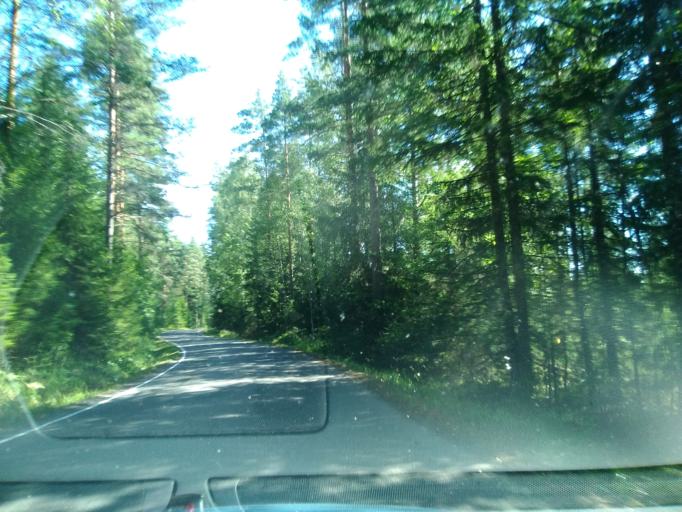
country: FI
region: Uusimaa
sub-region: Helsinki
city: Kaerkoelae
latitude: 60.7887
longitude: 24.0810
